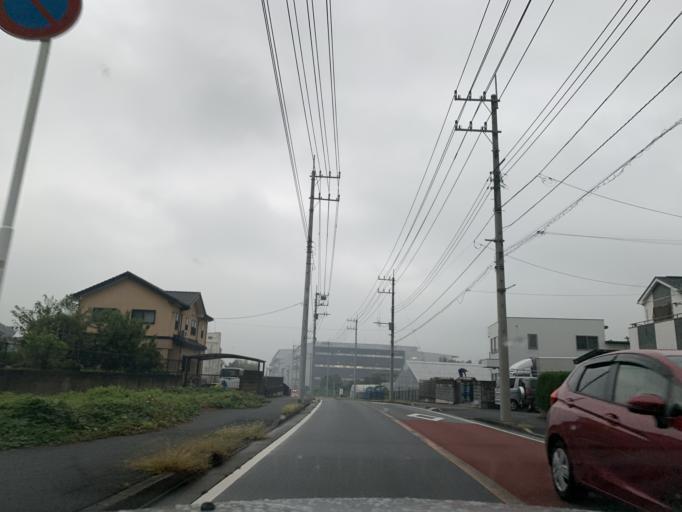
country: JP
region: Chiba
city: Noda
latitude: 35.9103
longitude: 139.8951
